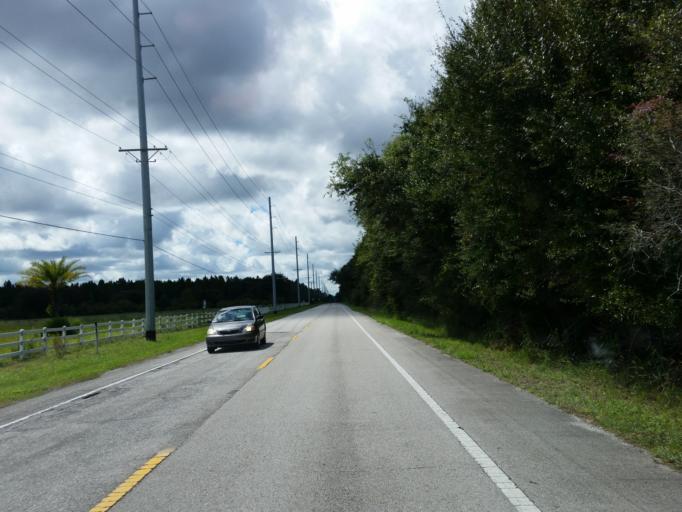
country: US
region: Florida
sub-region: Hillsborough County
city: Pebble Creek
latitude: 28.1595
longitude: -82.2700
